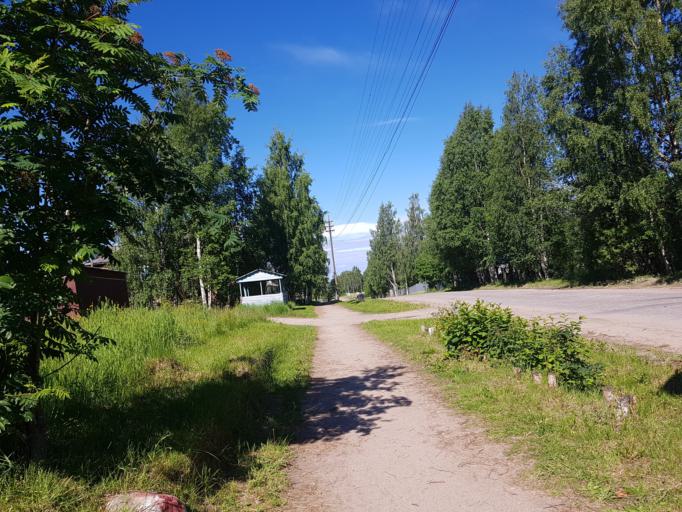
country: RU
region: Republic of Karelia
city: Kalevala
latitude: 65.1959
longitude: 31.2060
